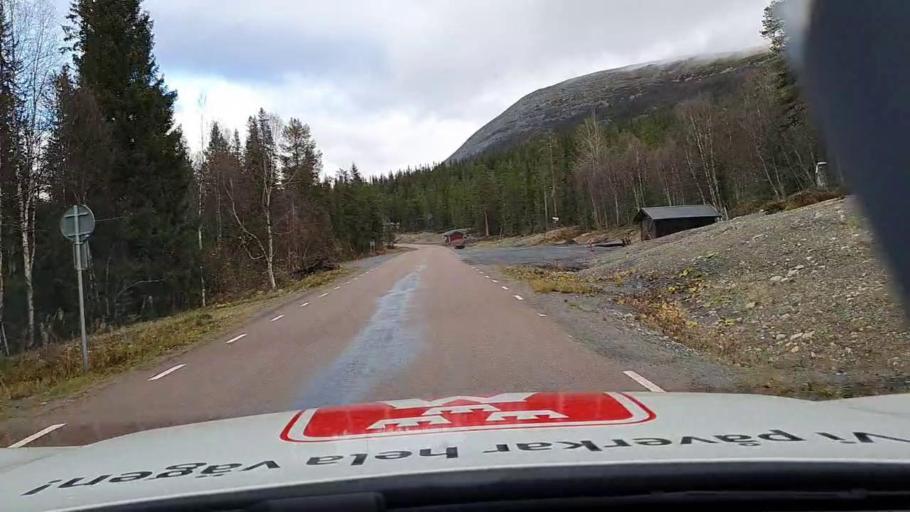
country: SE
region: Jaemtland
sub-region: Are Kommun
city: Jarpen
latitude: 63.0802
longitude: 13.7687
